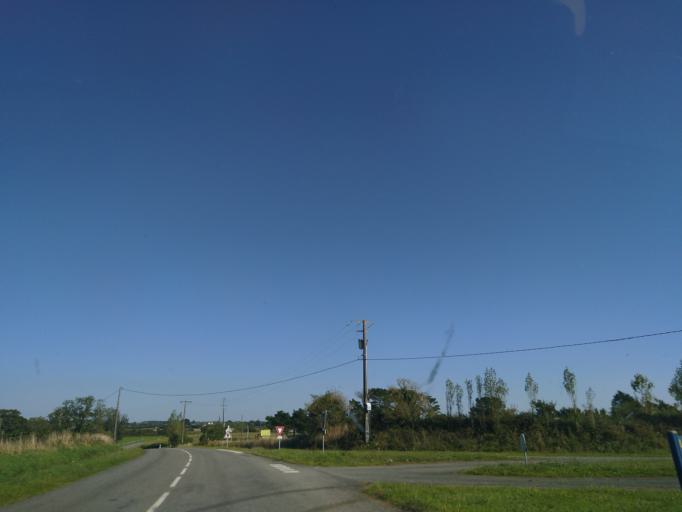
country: FR
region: Brittany
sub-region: Departement du Finistere
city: Le Faou
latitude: 48.2657
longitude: -4.2155
